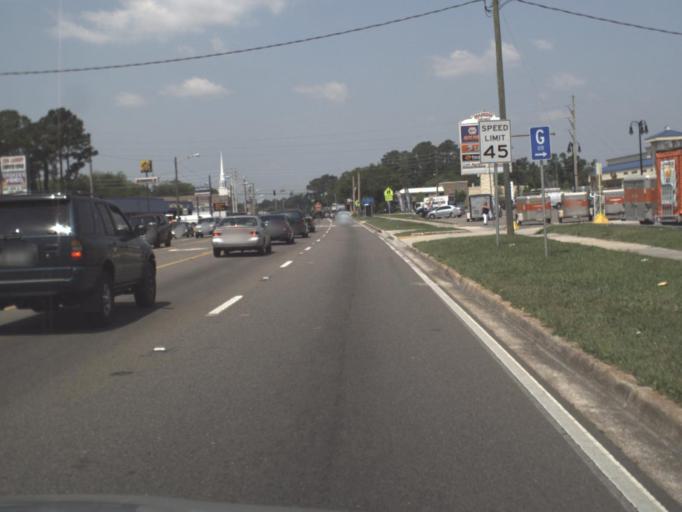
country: US
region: Florida
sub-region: Duval County
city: Jacksonville
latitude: 30.3089
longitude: -81.7412
